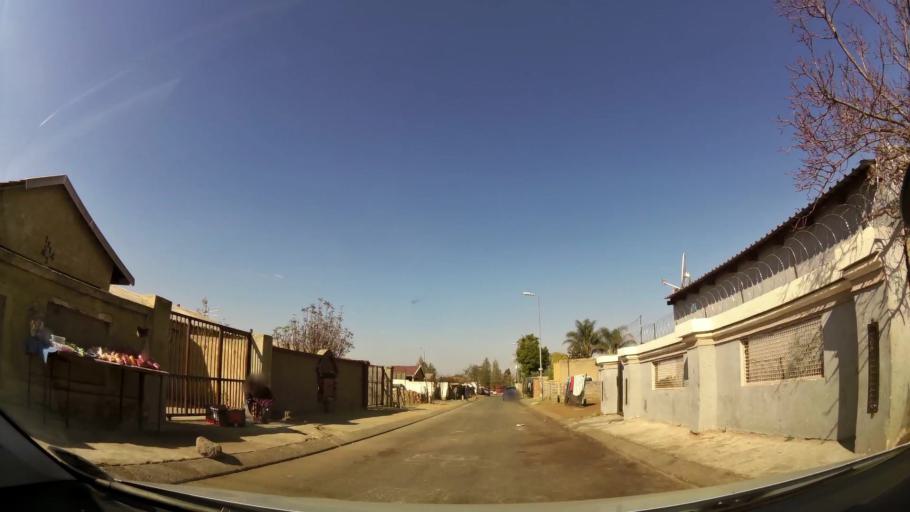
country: ZA
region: Gauteng
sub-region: City of Johannesburg Metropolitan Municipality
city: Soweto
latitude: -26.2805
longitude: 27.8656
